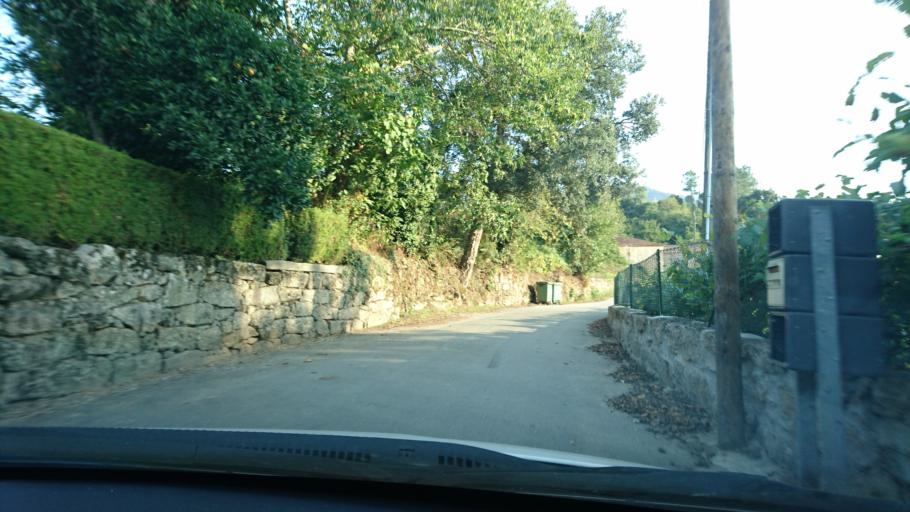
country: PT
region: Vila Real
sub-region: Mondim de Basto
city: Mondim de Basto
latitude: 41.4476
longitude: -7.9288
